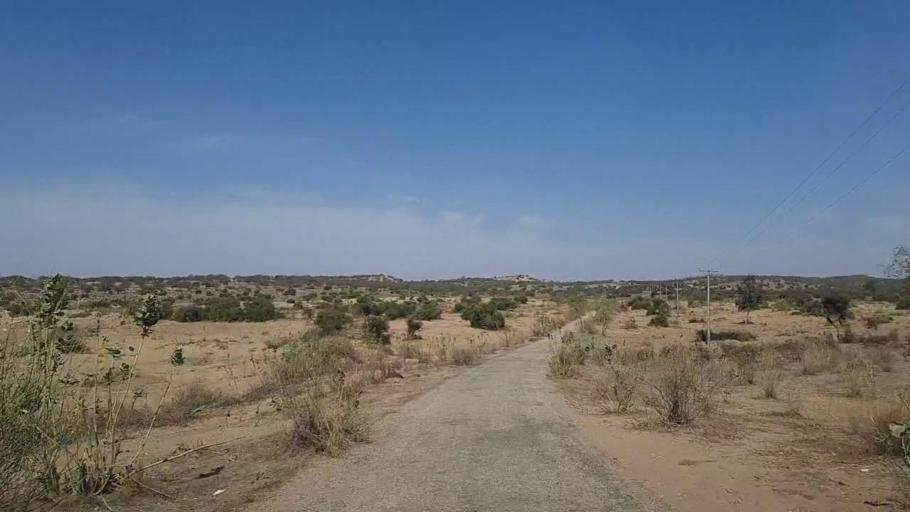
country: PK
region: Sindh
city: Mithi
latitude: 24.8435
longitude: 69.6676
